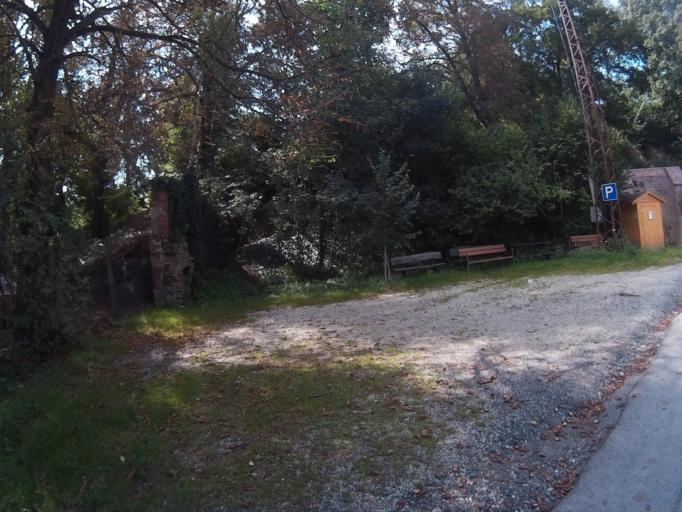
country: HU
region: Vas
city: Koszeg
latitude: 47.3965
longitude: 16.5362
